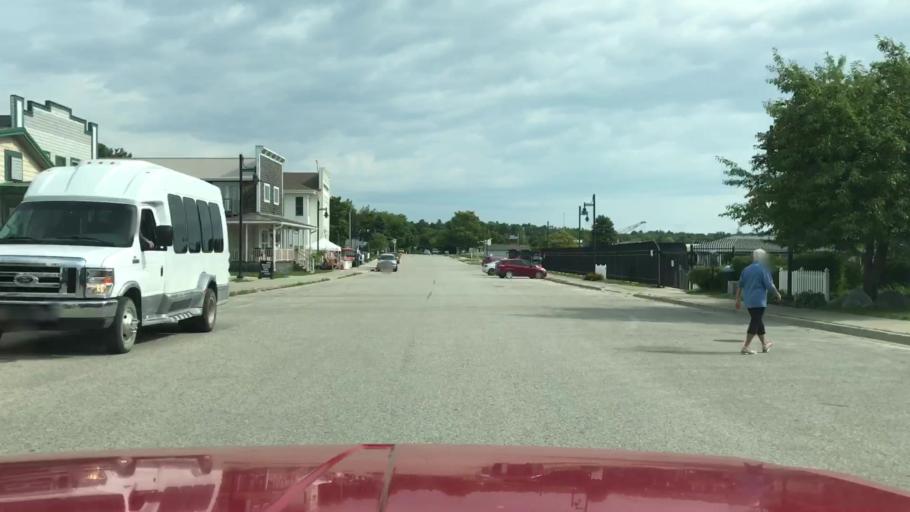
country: US
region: Michigan
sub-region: Charlevoix County
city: Charlevoix
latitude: 45.7466
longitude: -85.5201
